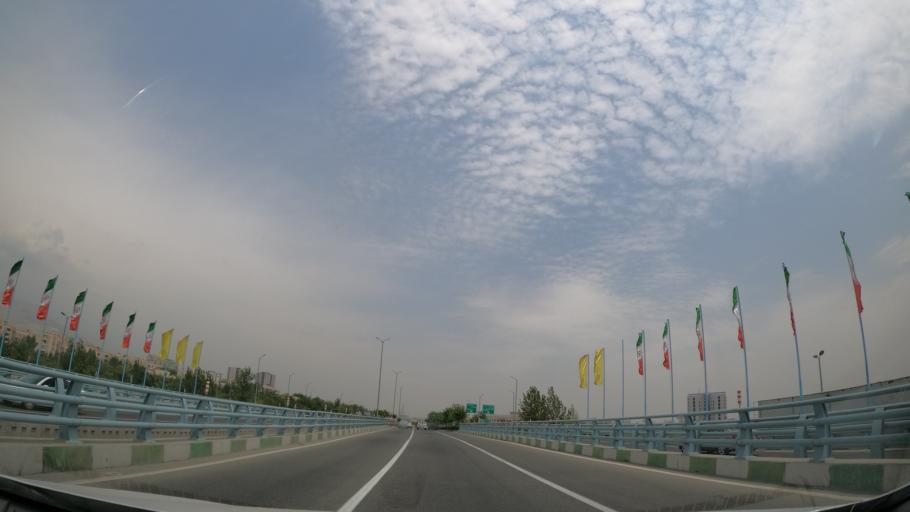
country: IR
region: Tehran
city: Shahr-e Qods
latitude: 35.7390
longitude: 51.2539
